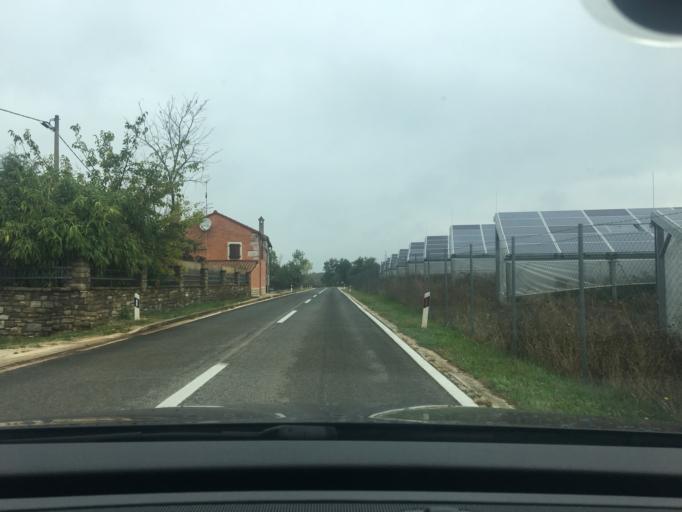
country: HR
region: Istarska
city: Buje
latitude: 45.4209
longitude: 13.6619
